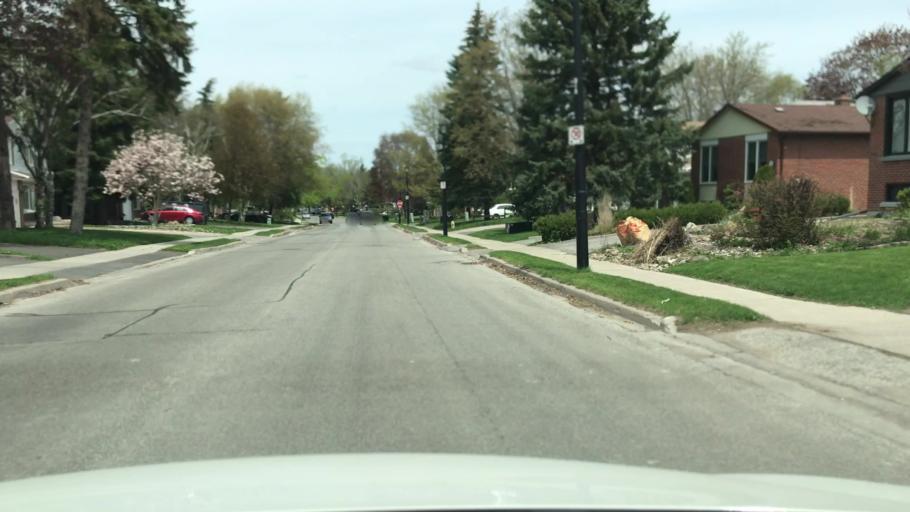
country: CA
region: Ontario
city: Newmarket
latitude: 44.0426
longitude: -79.4700
